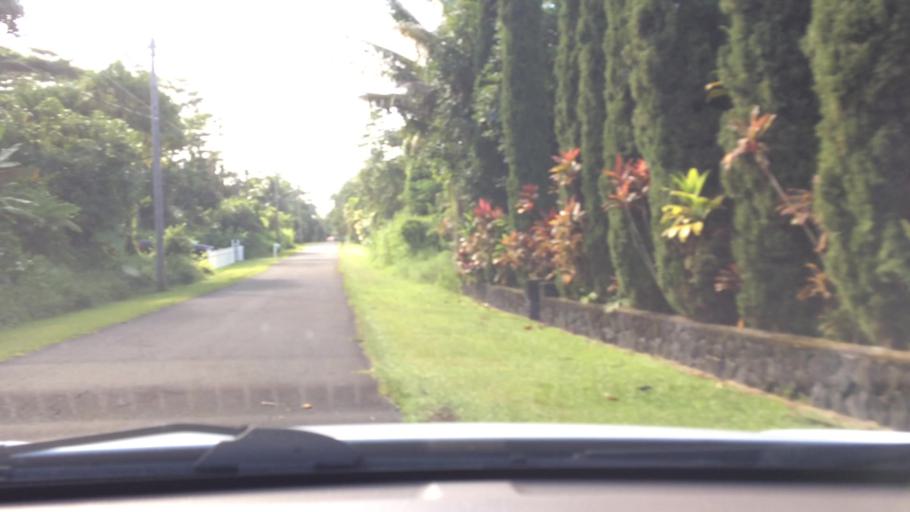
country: US
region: Hawaii
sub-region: Hawaii County
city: Hawaiian Beaches
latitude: 19.5435
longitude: -154.8978
